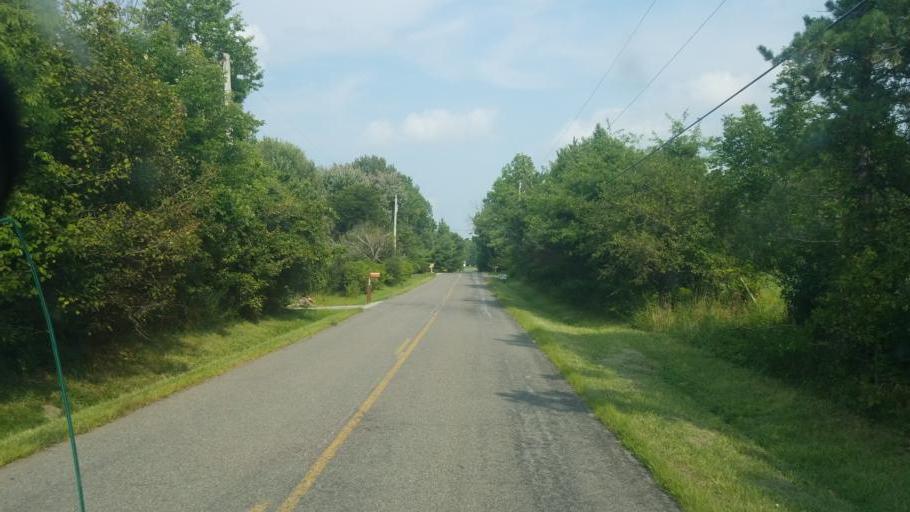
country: US
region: Ohio
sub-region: Medina County
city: Medina
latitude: 41.1577
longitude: -81.9816
